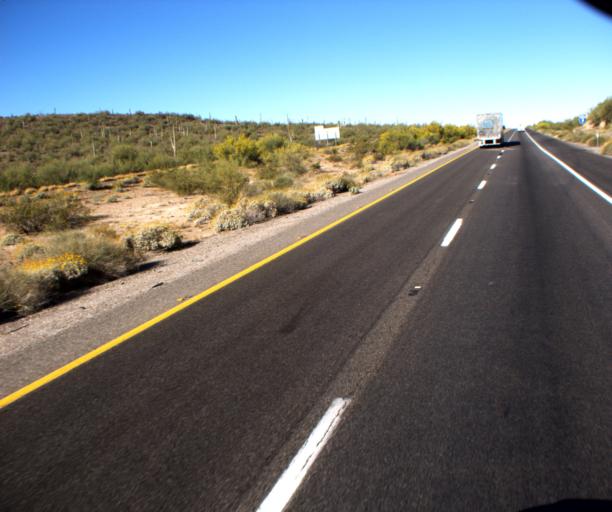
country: US
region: Arizona
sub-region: Pinal County
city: Maricopa
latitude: 32.8351
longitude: -112.1518
